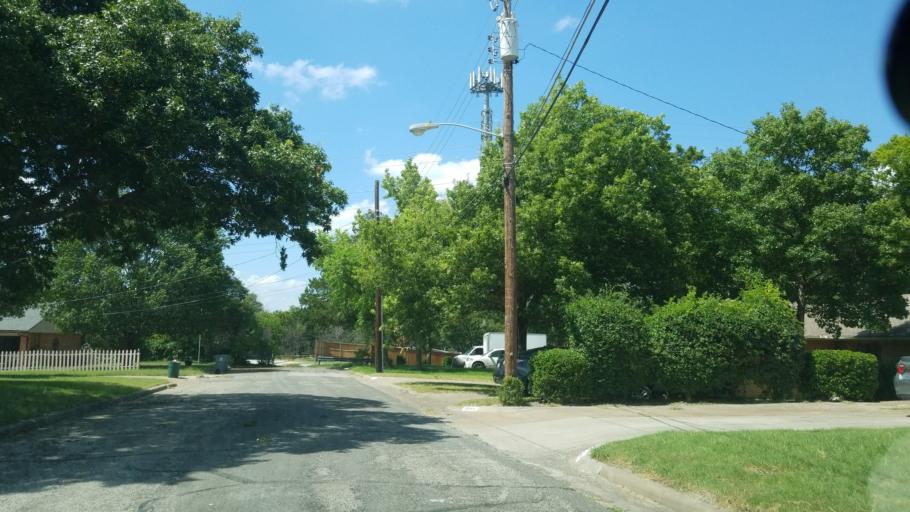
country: US
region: Texas
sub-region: Dallas County
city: Balch Springs
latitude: 32.7602
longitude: -96.6954
